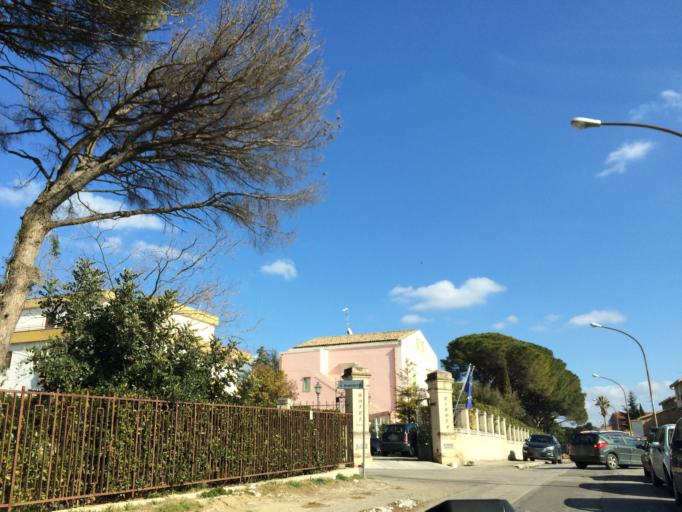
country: IT
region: Basilicate
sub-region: Provincia di Matera
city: Matera
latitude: 40.6582
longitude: 16.6105
